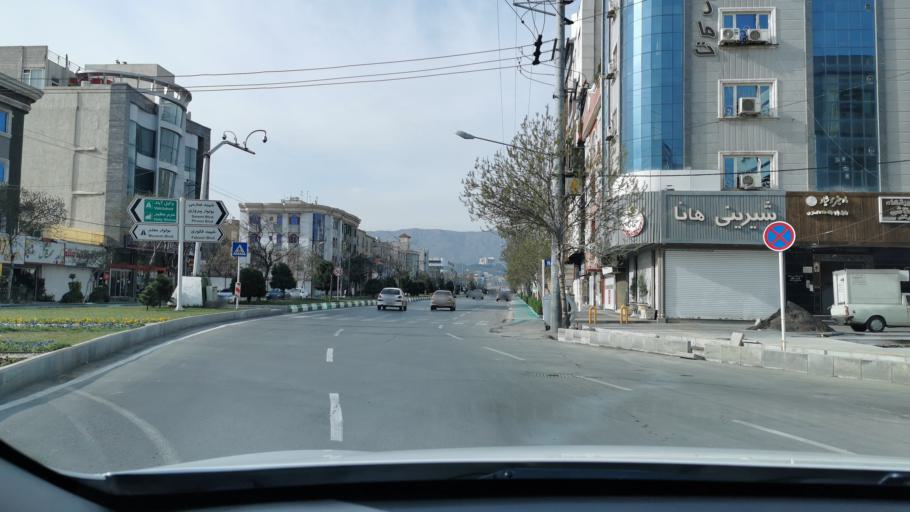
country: IR
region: Razavi Khorasan
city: Mashhad
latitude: 36.3191
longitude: 59.5118
